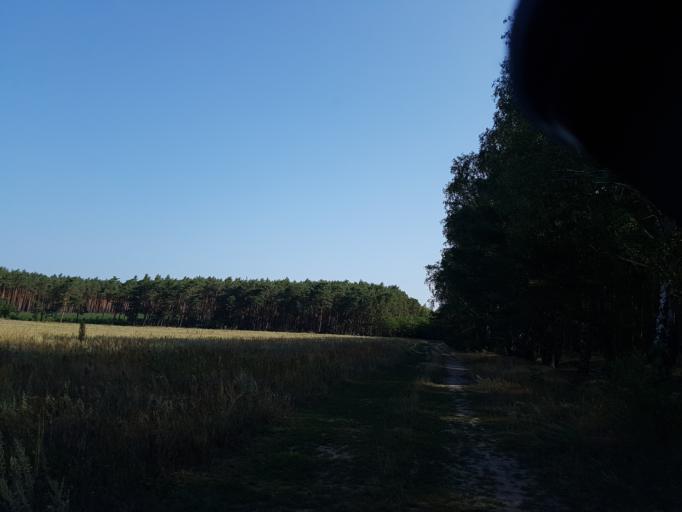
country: DE
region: Brandenburg
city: Wollin
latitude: 52.2476
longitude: 12.5082
